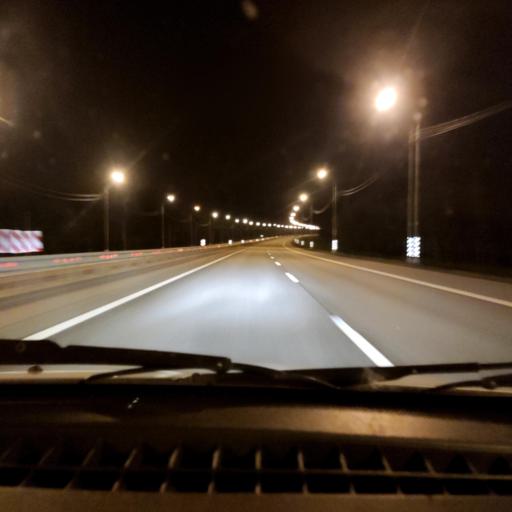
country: RU
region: Lipetsk
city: Zadonsk
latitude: 52.3798
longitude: 38.8801
